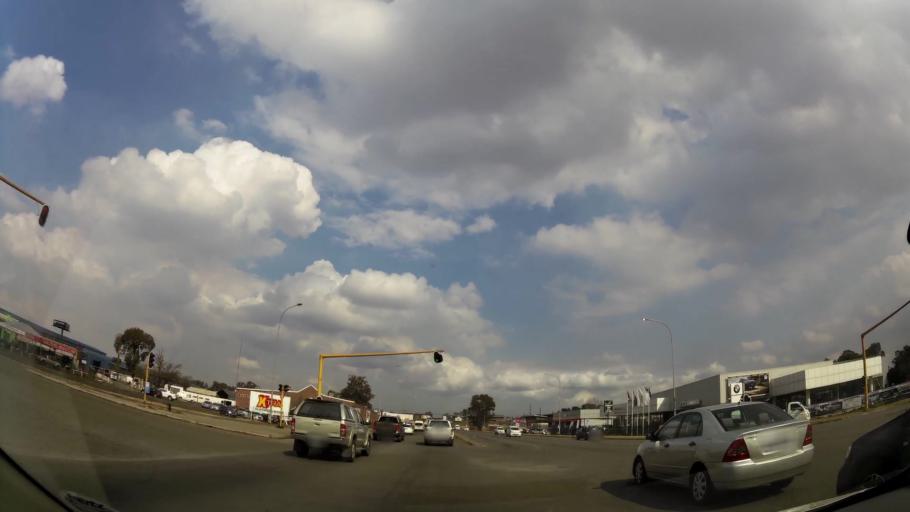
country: ZA
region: Gauteng
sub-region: Sedibeng District Municipality
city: Vereeniging
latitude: -26.6620
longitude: 27.9345
